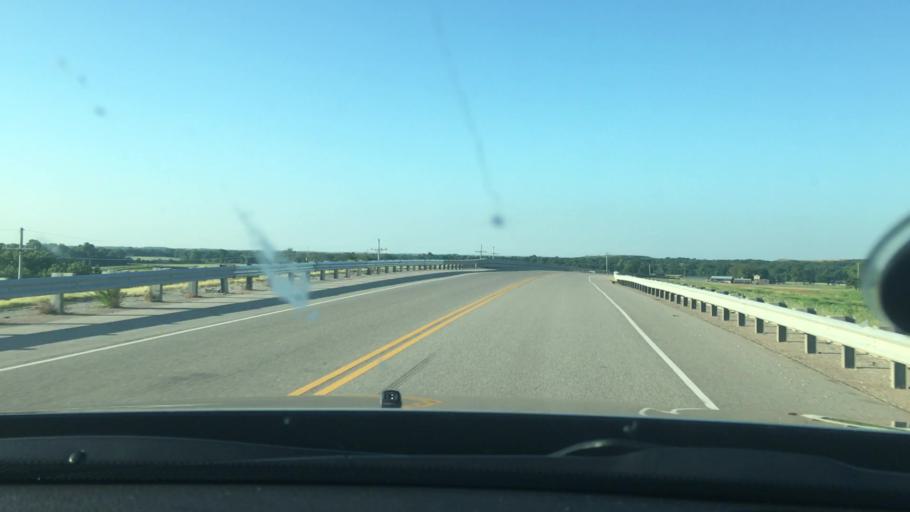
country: US
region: Oklahoma
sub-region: Pontotoc County
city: Ada
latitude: 34.6537
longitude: -96.7954
